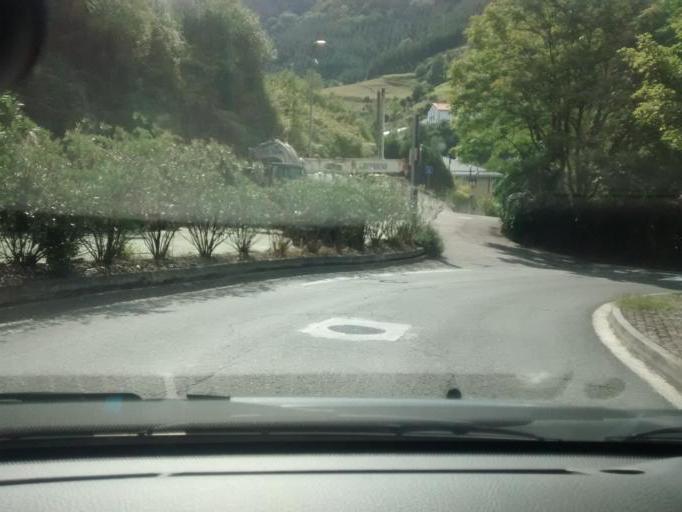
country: ES
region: Basque Country
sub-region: Provincia de Guipuzcoa
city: Eibar
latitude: 43.1919
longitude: -2.4513
